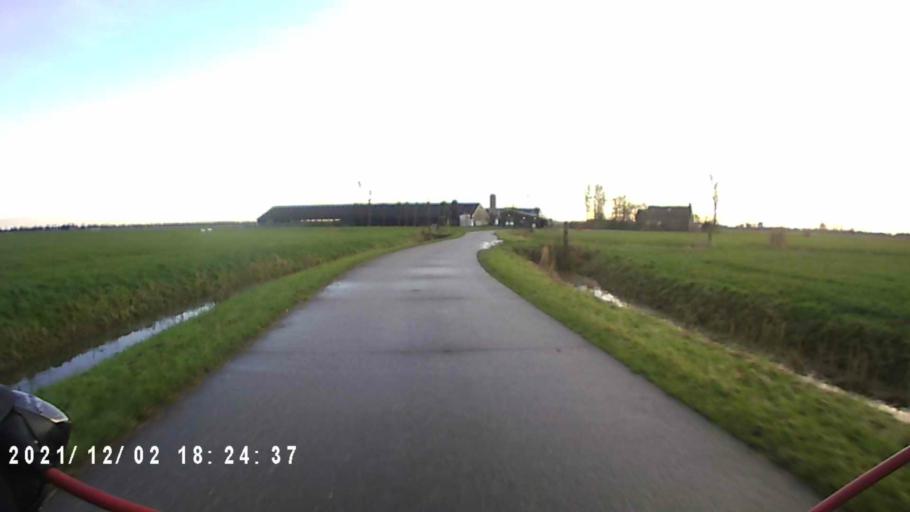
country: NL
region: Groningen
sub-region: Gemeente Groningen
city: Korrewegwijk
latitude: 53.2747
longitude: 6.5460
